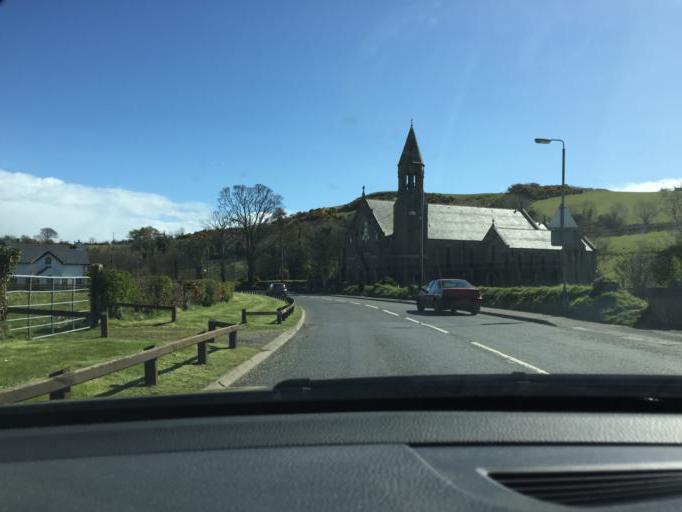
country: GB
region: Northern Ireland
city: Cushendall
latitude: 55.0803
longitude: -6.0712
